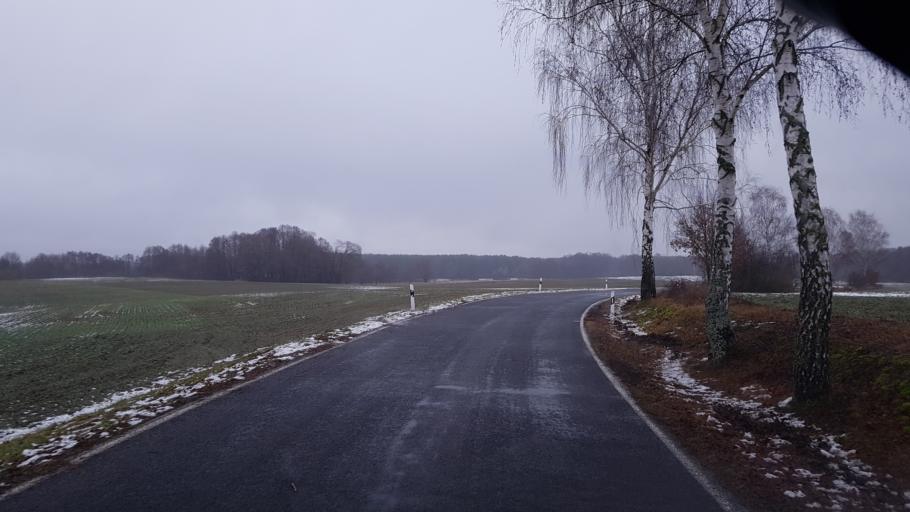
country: DE
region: Brandenburg
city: Lieberose
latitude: 51.9774
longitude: 14.3213
